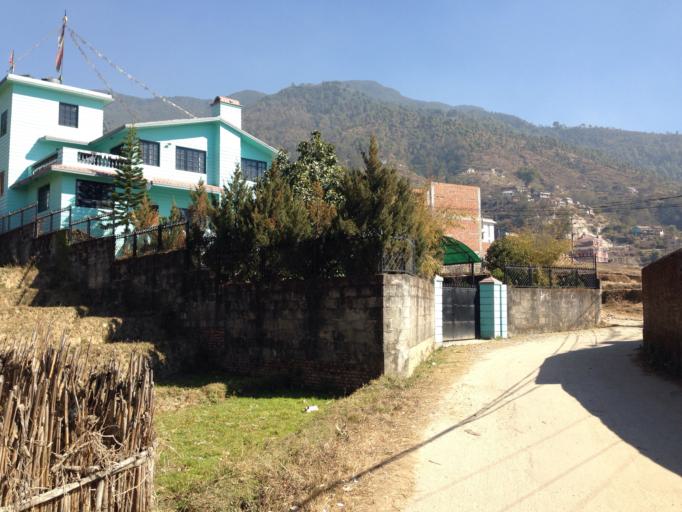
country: NP
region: Central Region
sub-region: Bagmati Zone
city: Kathmandu
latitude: 27.7780
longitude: 85.3679
